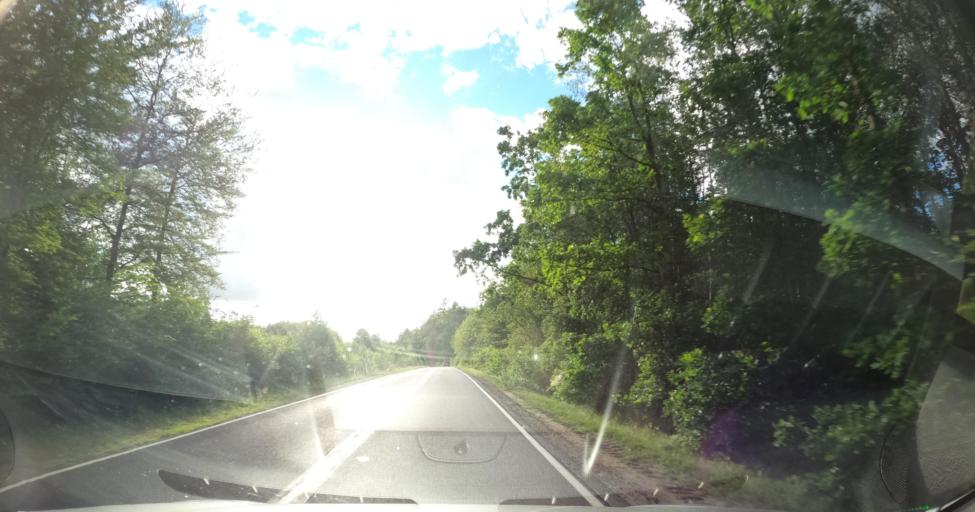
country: PL
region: Pomeranian Voivodeship
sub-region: Powiat slupski
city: Potegowo
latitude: 54.4083
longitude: 17.4419
